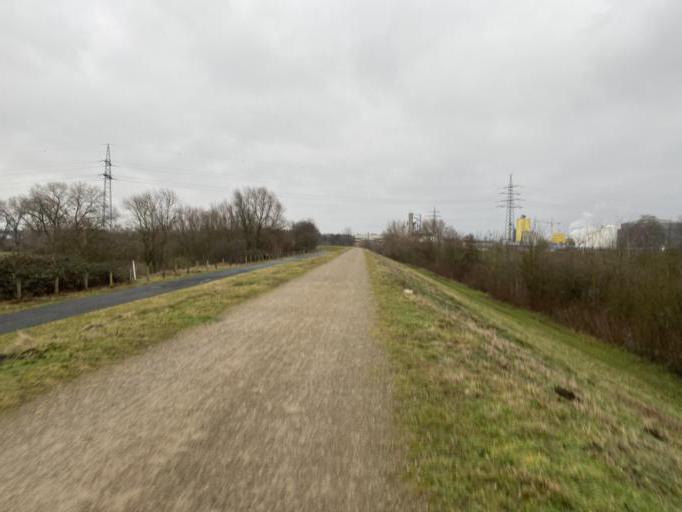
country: DE
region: North Rhine-Westphalia
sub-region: Regierungsbezirk Arnsberg
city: Hamm
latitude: 51.6793
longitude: 7.7672
